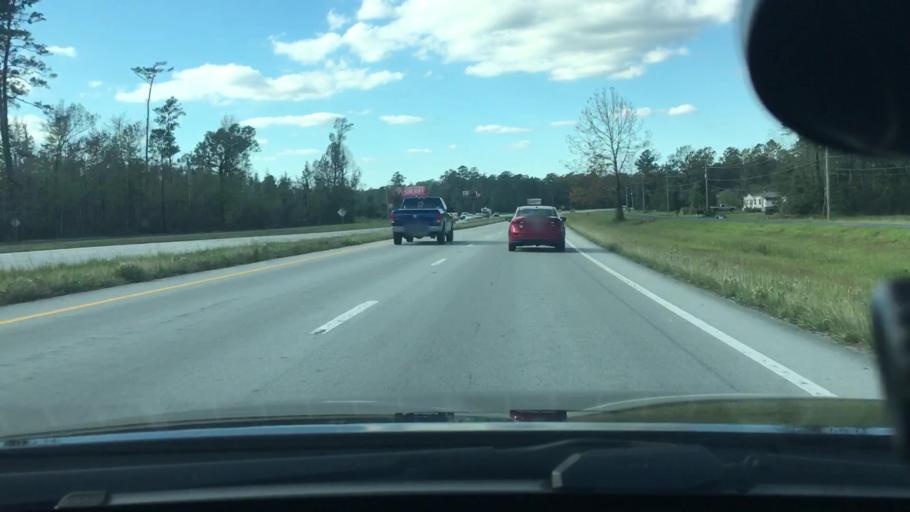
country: US
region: North Carolina
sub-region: Craven County
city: Neuse Forest
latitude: 34.9695
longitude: -76.9693
